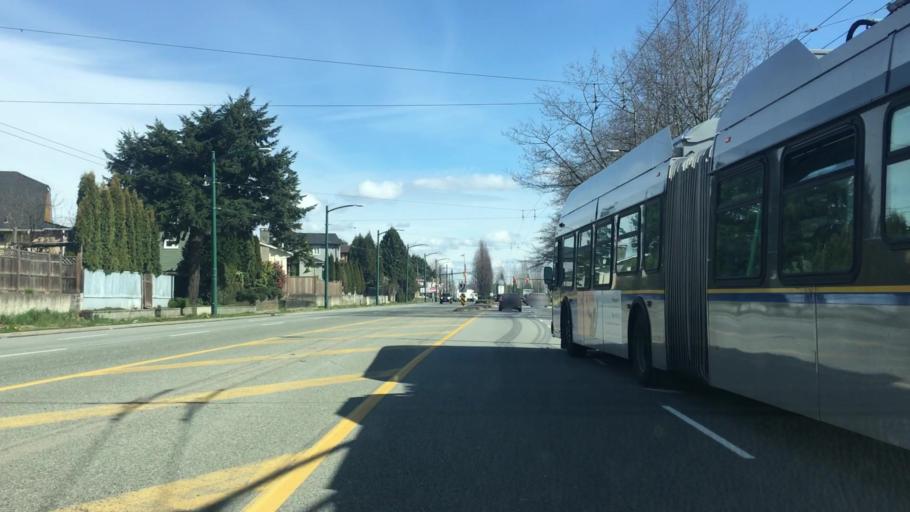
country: CA
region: British Columbia
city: Vancouver
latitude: 49.2120
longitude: -123.1052
